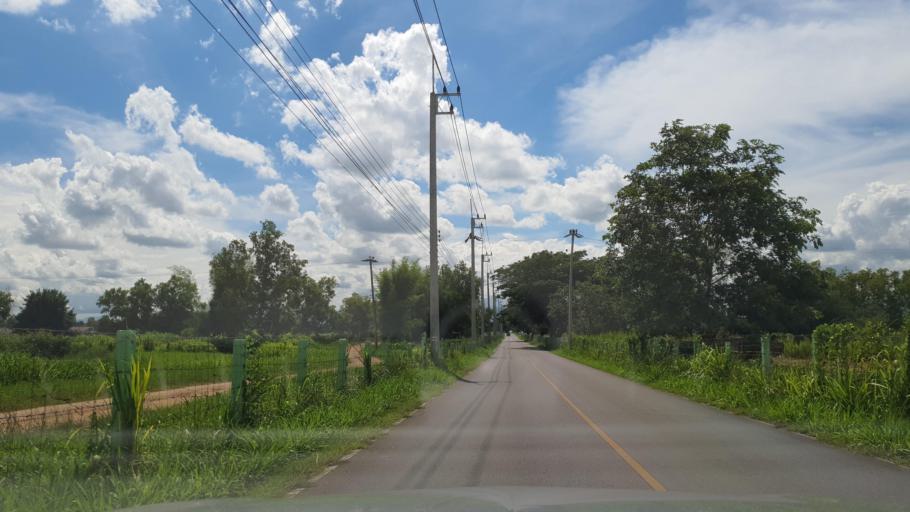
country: TH
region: Chiang Mai
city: San Pa Tong
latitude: 18.5940
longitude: 98.8683
